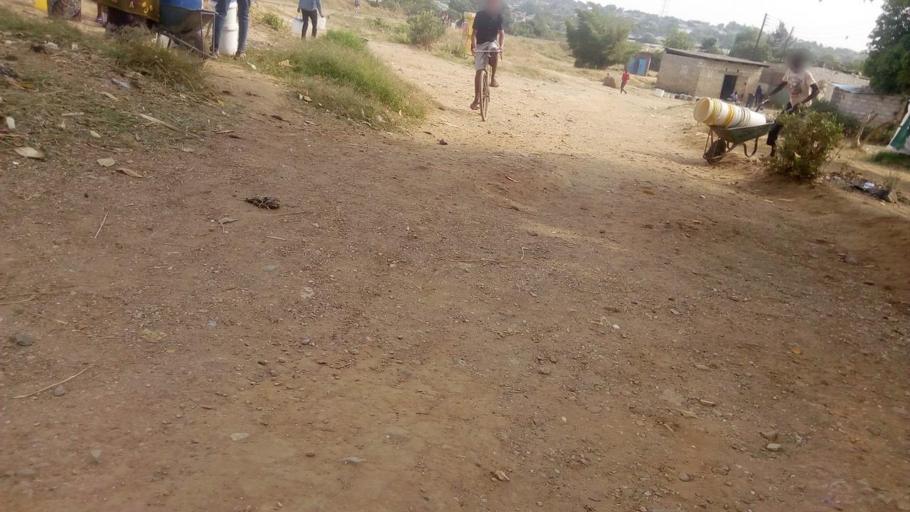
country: ZM
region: Lusaka
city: Lusaka
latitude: -15.3613
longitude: 28.3049
